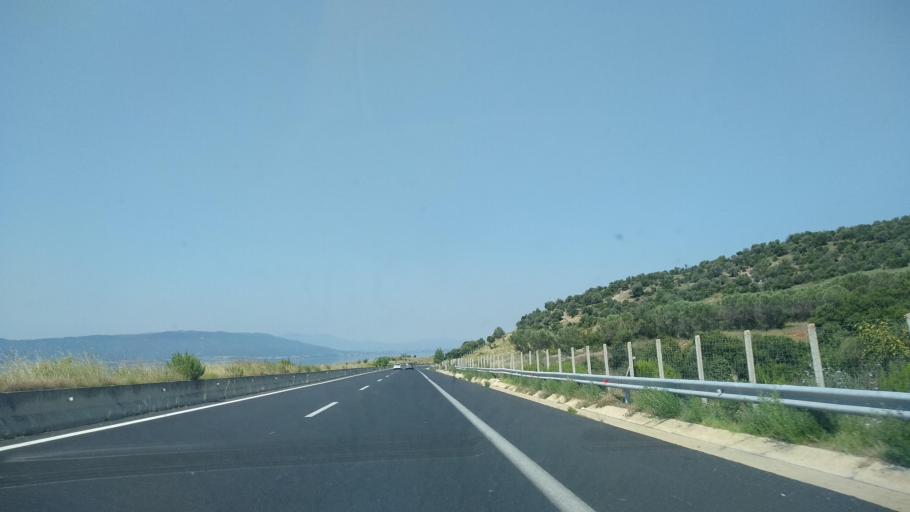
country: GR
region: Central Macedonia
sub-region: Nomos Thessalonikis
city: Nea Apollonia
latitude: 40.6927
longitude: 23.4756
